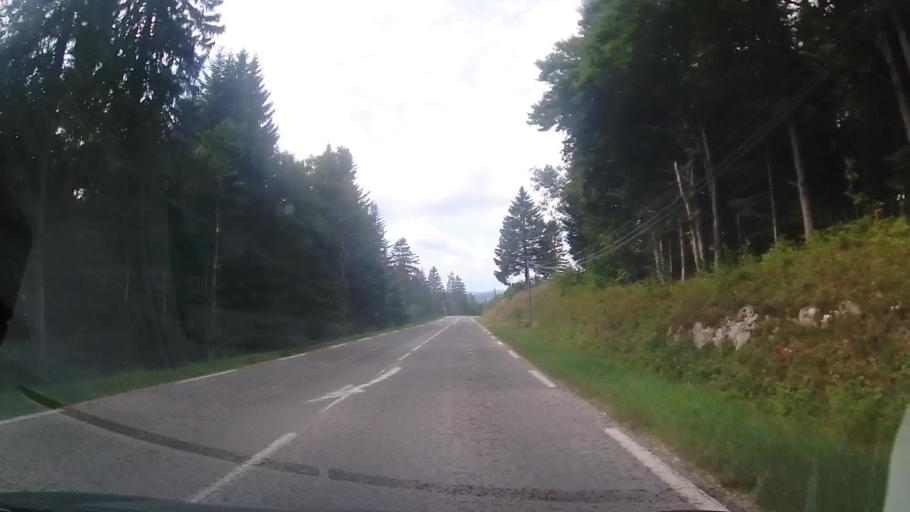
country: FR
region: Franche-Comte
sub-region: Departement du Jura
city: Les Rousses
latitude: 46.4504
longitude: 6.0737
